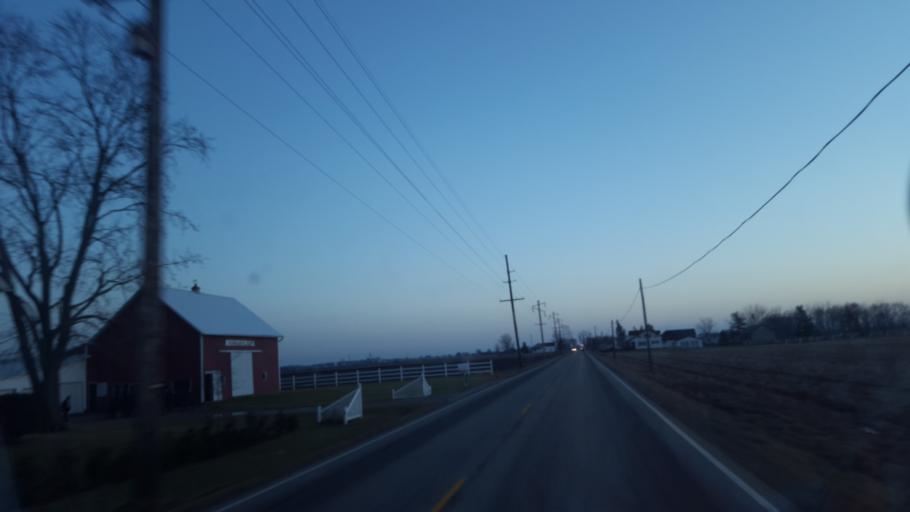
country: US
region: Indiana
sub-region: Elkhart County
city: Nappanee
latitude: 41.3712
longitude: -86.0007
